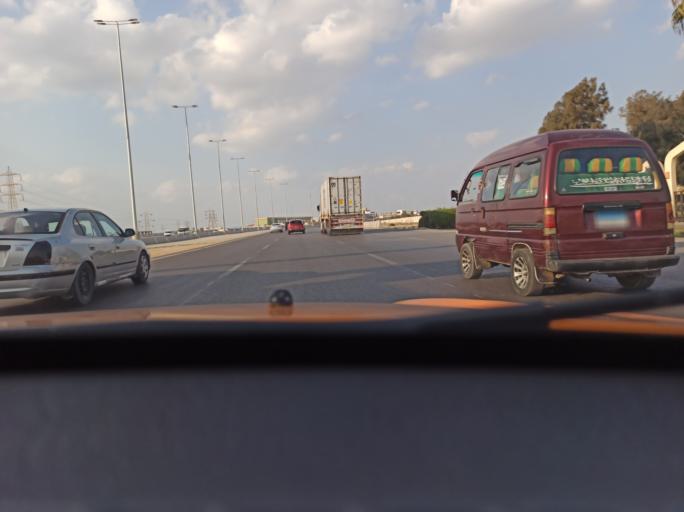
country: EG
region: Al Isma'iliyah
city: Ismailia
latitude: 30.5920
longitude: 32.2002
